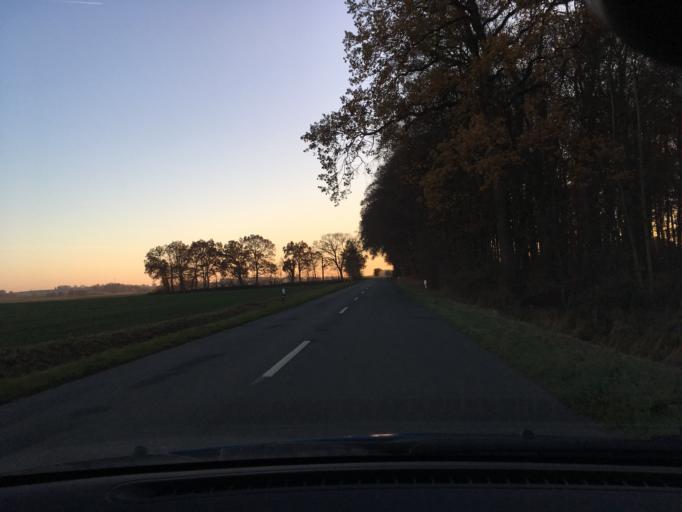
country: DE
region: Lower Saxony
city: Natendorf
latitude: 53.0769
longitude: 10.4631
